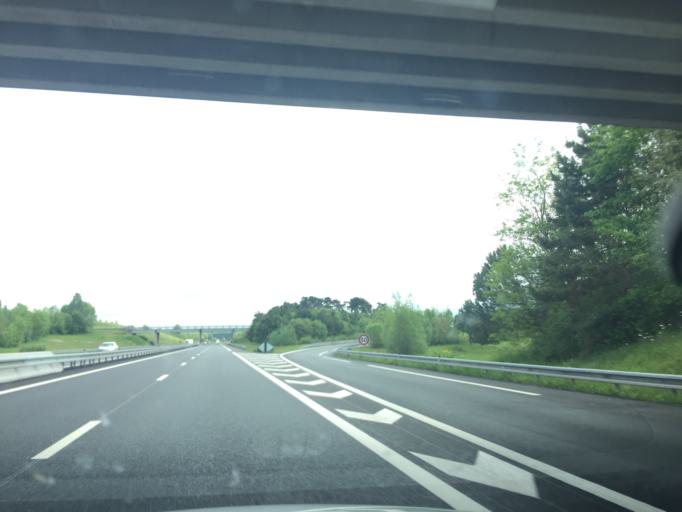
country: FR
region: Pays de la Loire
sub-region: Departement de la Sarthe
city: Ecommoy
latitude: 47.8238
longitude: 0.3067
